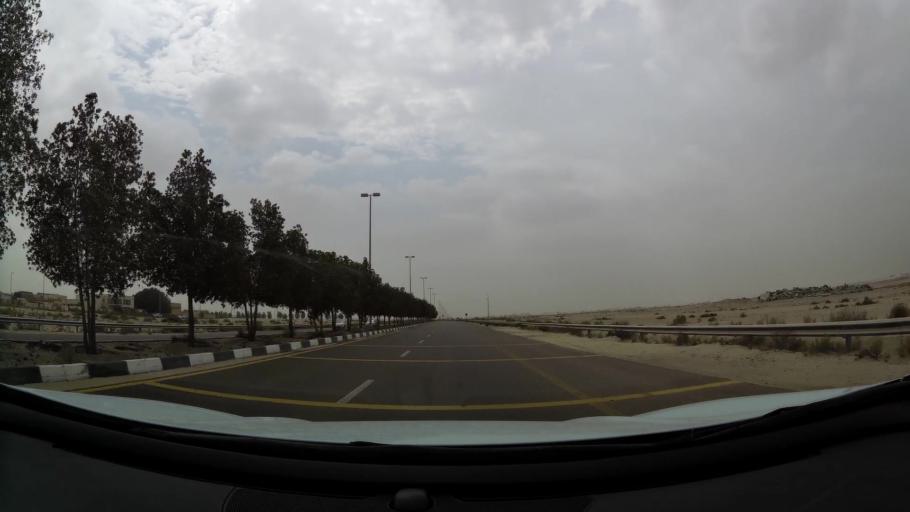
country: AE
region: Abu Dhabi
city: Abu Dhabi
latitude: 24.3890
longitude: 54.6807
